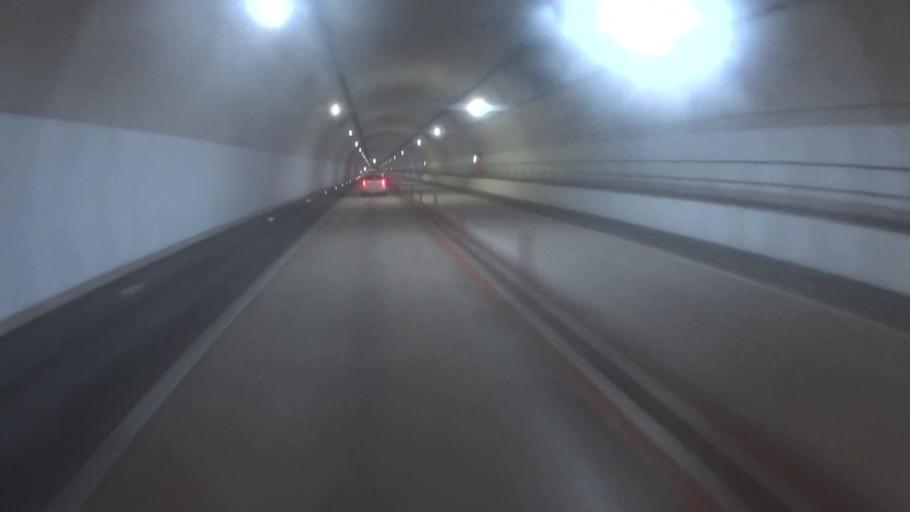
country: JP
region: Kyoto
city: Ayabe
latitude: 35.3293
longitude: 135.3129
